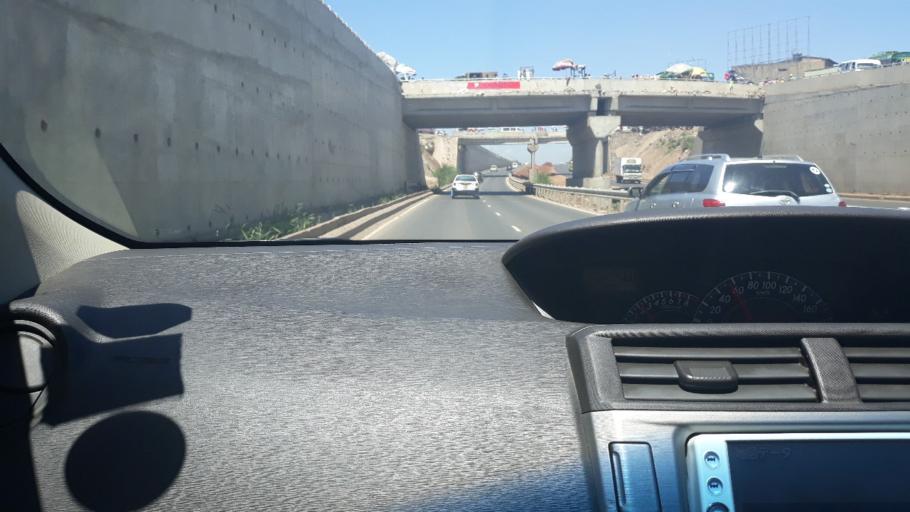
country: KE
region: Nairobi Area
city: Pumwani
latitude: -1.2633
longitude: 36.8791
